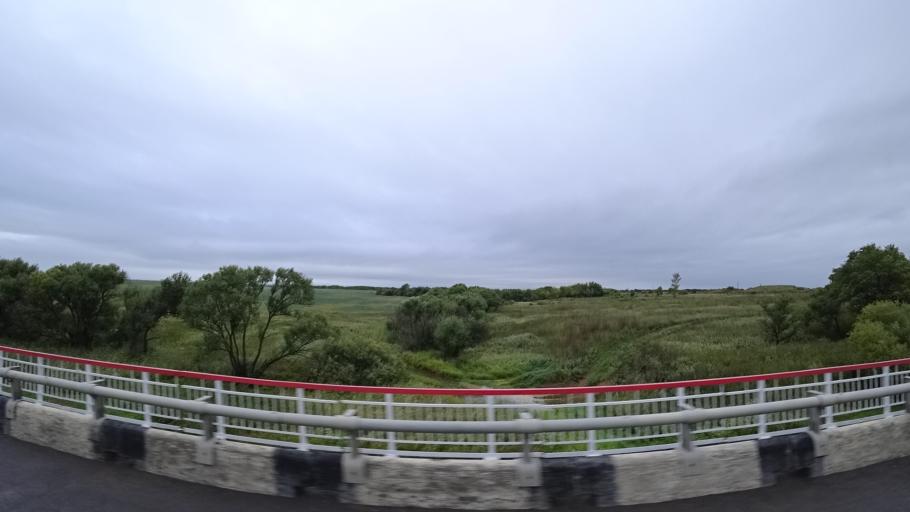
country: RU
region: Primorskiy
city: Chernigovka
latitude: 44.3093
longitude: 132.5434
